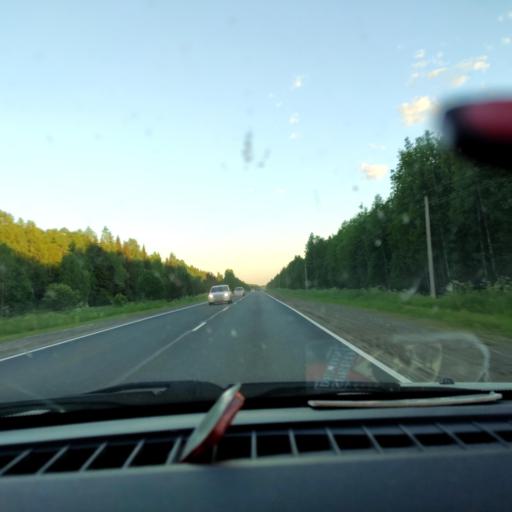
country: RU
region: Perm
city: Karagay
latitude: 58.3993
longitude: 54.8575
